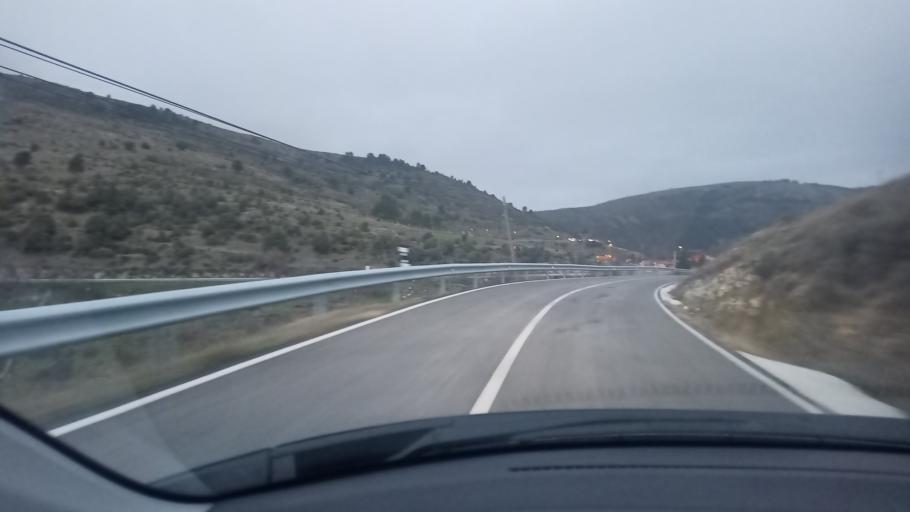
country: ES
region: Madrid
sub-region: Provincia de Madrid
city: Zarzalejo
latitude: 40.5567
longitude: -4.1965
